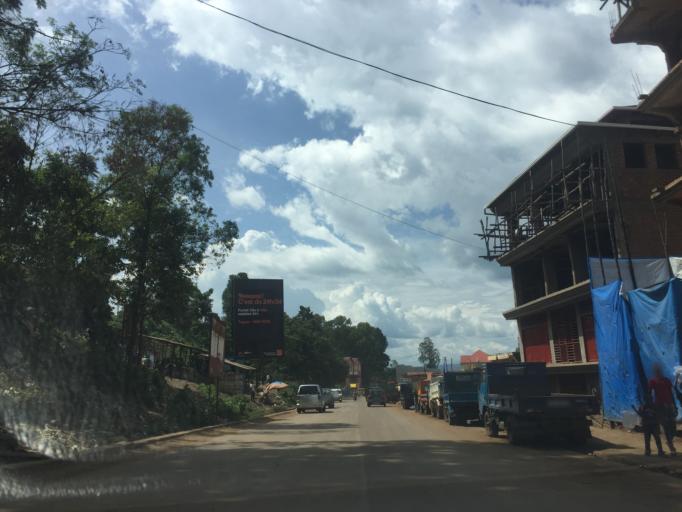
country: CD
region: South Kivu
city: Bukavu
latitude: -2.4926
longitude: 28.8491
